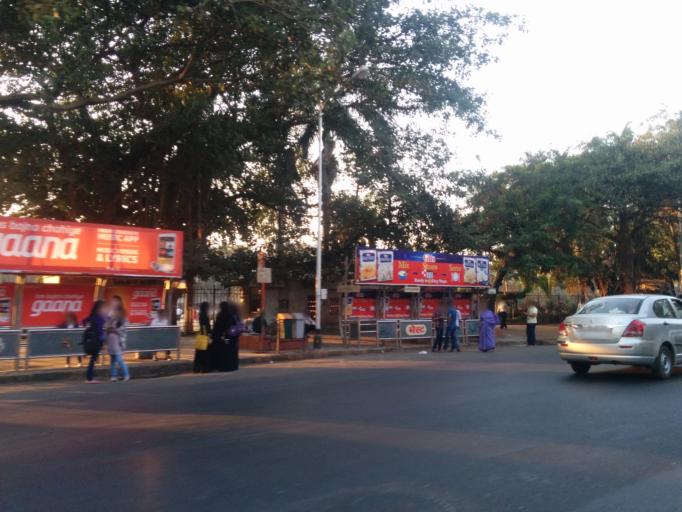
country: IN
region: Maharashtra
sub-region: Raigarh
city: Uran
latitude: 18.9293
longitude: 72.8297
